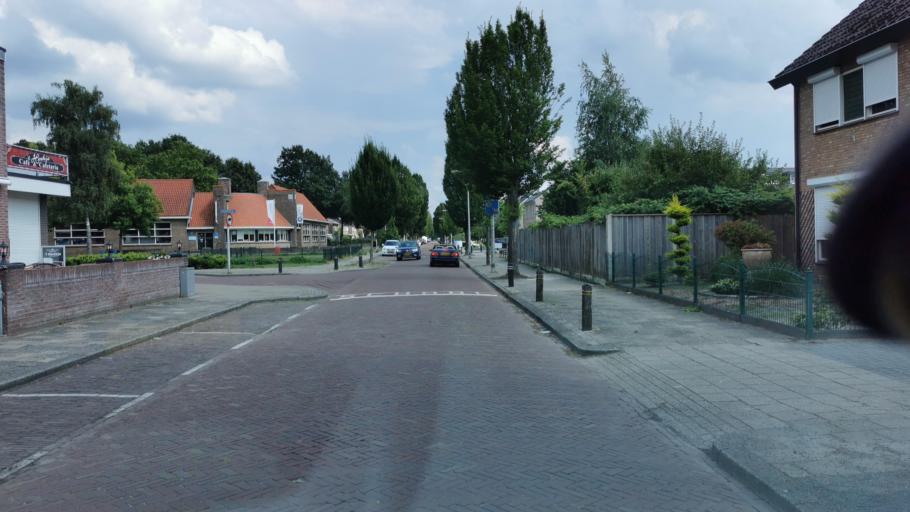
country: NL
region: Overijssel
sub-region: Gemeente Losser
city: Losser
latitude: 52.2208
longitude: 6.9642
